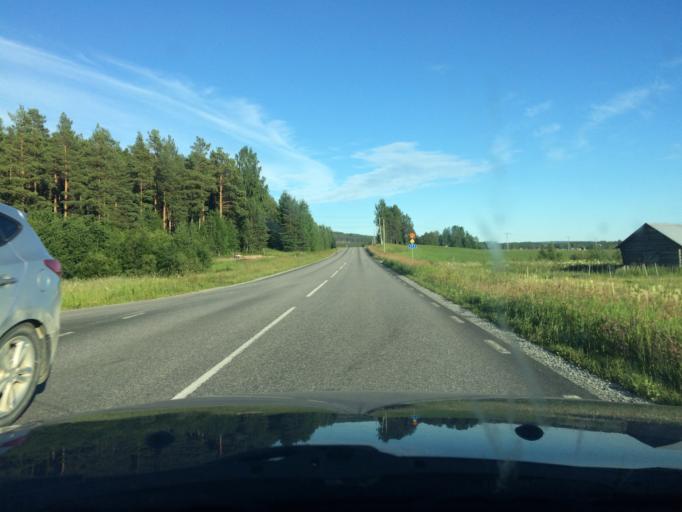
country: SE
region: Norrbotten
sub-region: Pitea Kommun
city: Roknas
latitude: 65.3262
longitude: 21.2204
